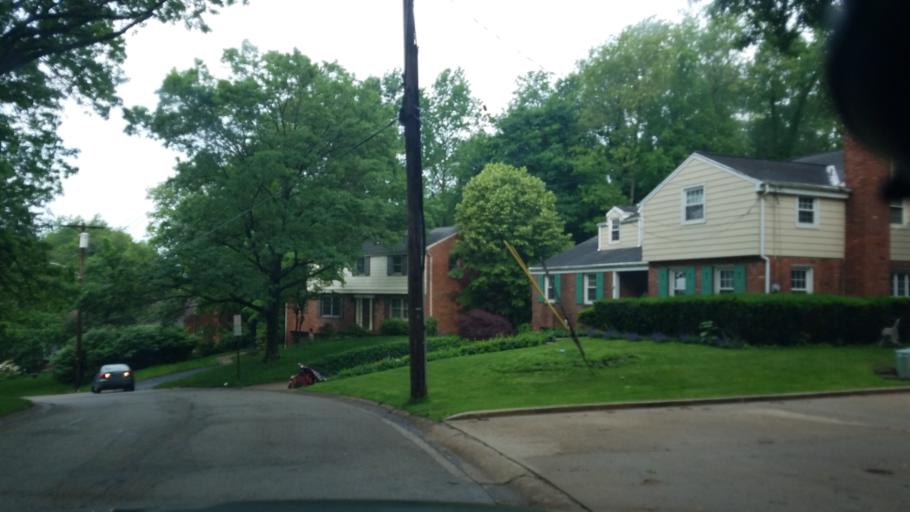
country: US
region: Pennsylvania
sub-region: Allegheny County
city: Edgewood
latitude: 40.4346
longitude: -79.8755
